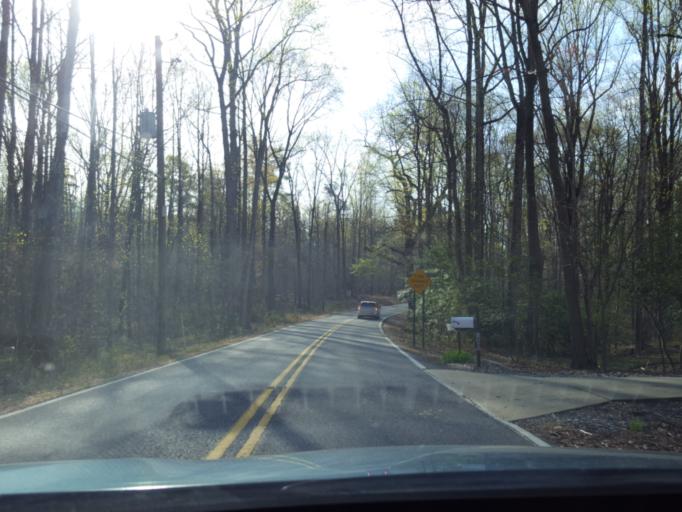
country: US
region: Maryland
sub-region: Prince George's County
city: Croom
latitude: 38.7582
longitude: -76.7278
